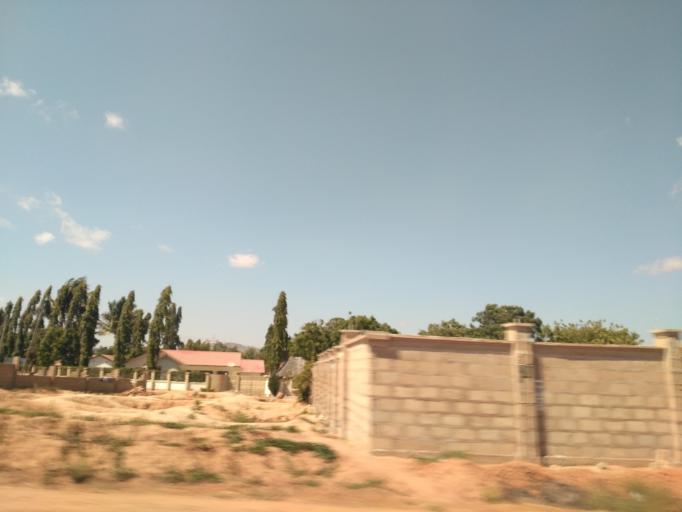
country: TZ
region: Dodoma
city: Dodoma
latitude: -6.1589
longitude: 35.7582
